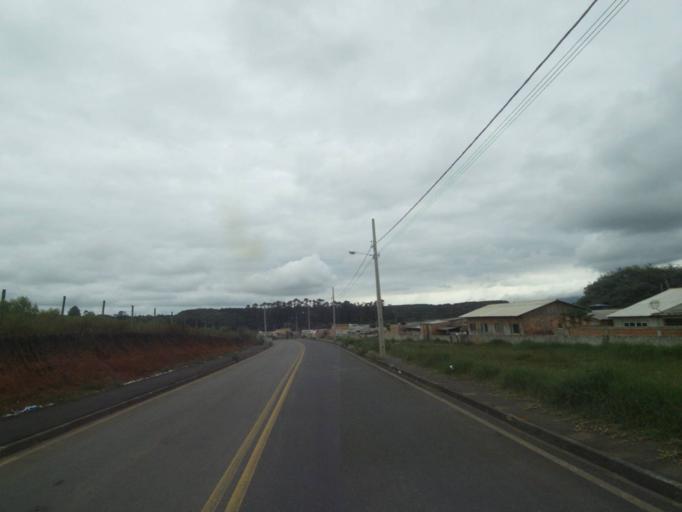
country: BR
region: Parana
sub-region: Quatro Barras
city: Quatro Barras
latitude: -25.3492
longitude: -49.1144
